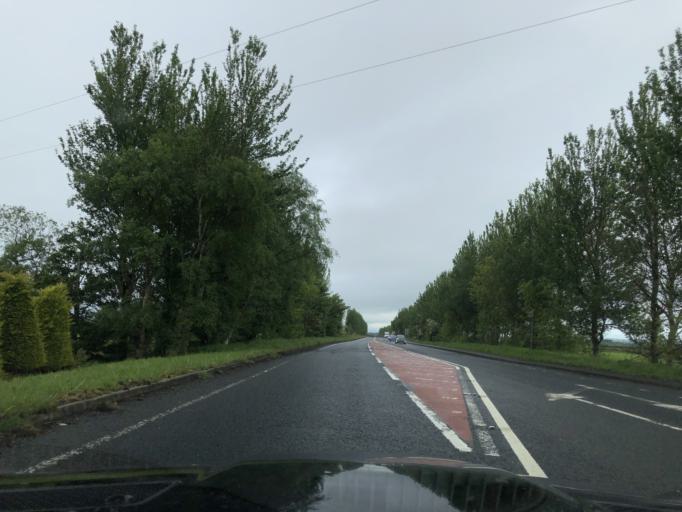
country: GB
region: Northern Ireland
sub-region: Ballymoney District
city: Ballymoney
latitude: 55.0574
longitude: -6.4608
